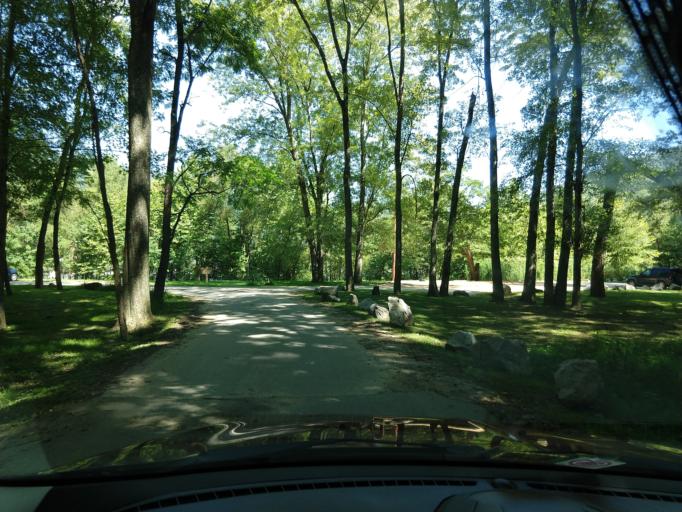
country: US
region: West Virginia
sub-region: Fayette County
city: Ansted
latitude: 38.1459
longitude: -81.2131
